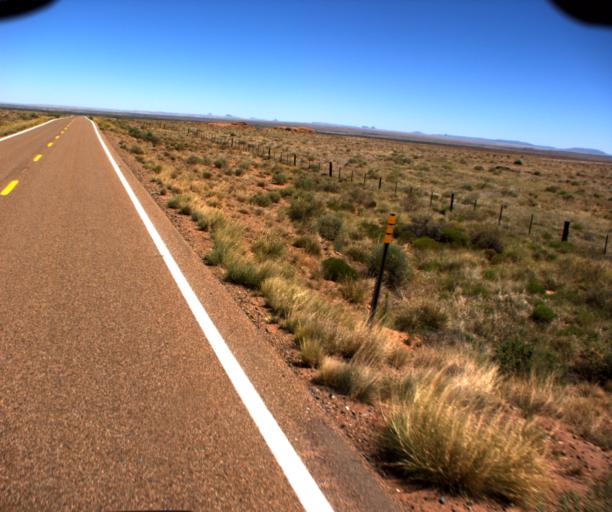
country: US
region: Arizona
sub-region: Navajo County
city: Winslow
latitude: 34.9238
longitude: -110.6378
